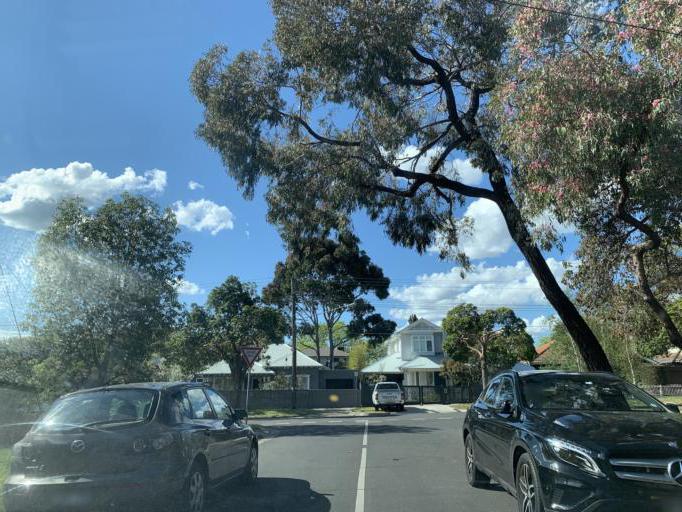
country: AU
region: Victoria
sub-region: Bayside
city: Hampton East
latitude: -37.9508
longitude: 145.0179
